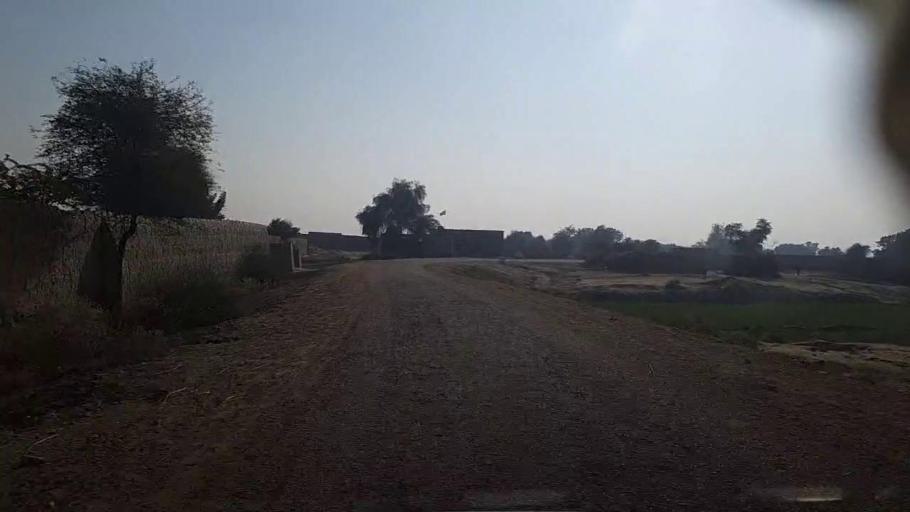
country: PK
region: Sindh
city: Kandiari
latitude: 26.7914
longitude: 68.4825
